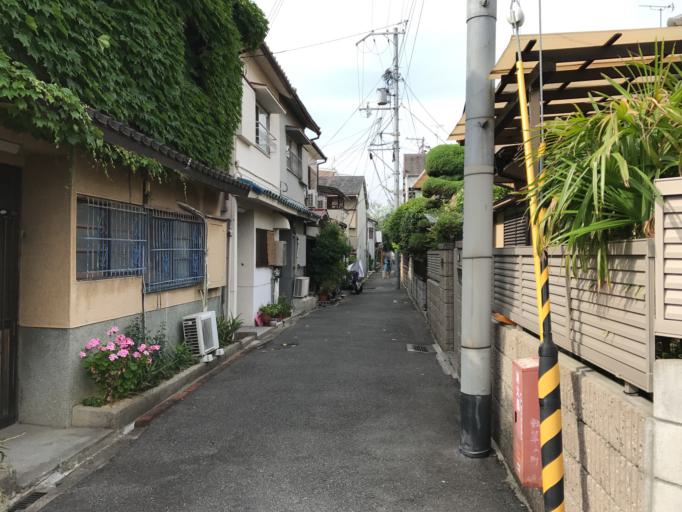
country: JP
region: Osaka
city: Daitocho
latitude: 34.6613
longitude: 135.6429
